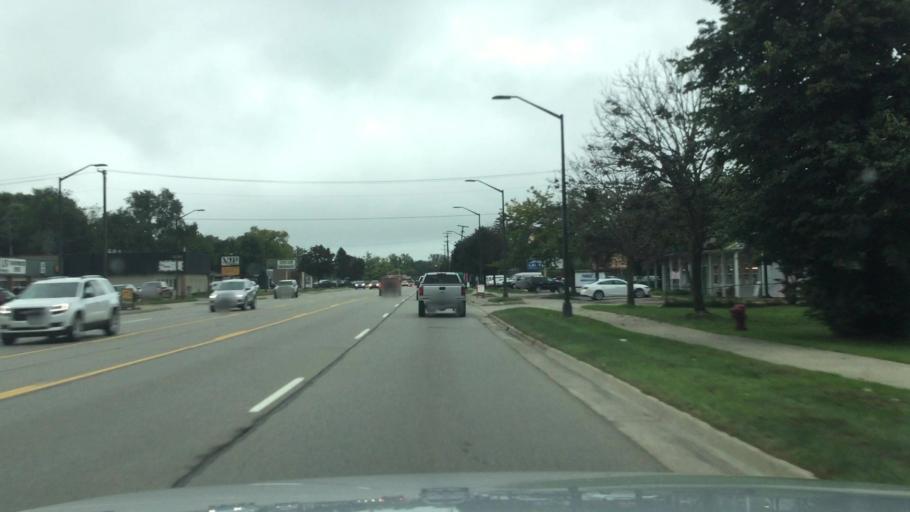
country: US
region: Michigan
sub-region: Oakland County
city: Waterford
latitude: 42.7068
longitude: -83.4054
